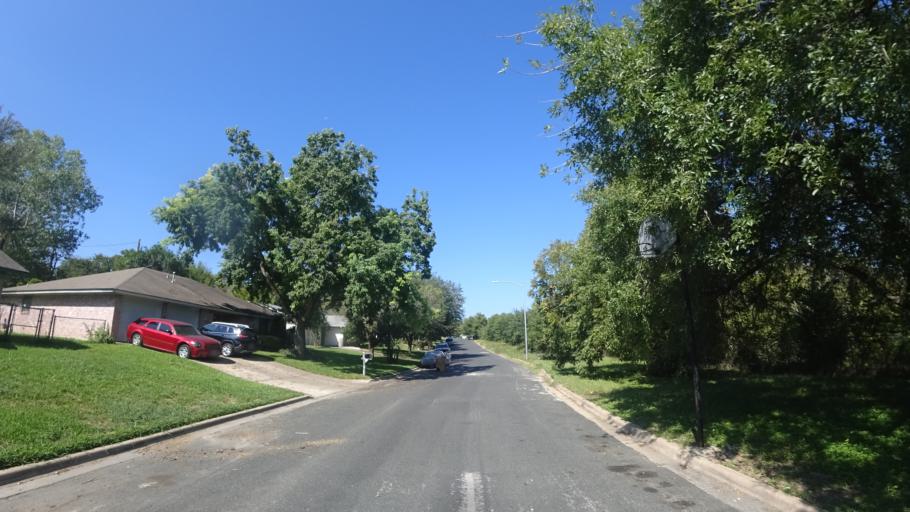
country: US
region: Texas
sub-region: Travis County
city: Austin
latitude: 30.3105
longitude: -97.6701
